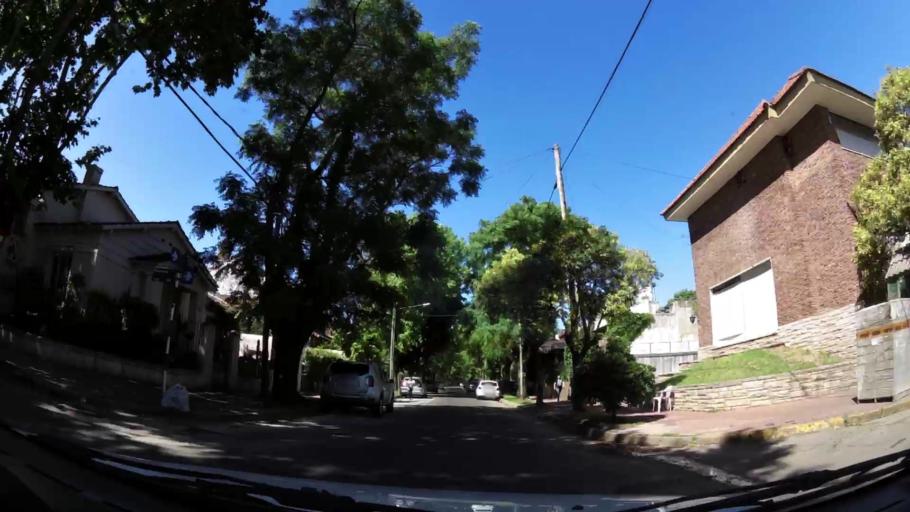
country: AR
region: Buenos Aires
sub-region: Partido de San Isidro
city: San Isidro
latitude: -34.4611
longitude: -58.5216
